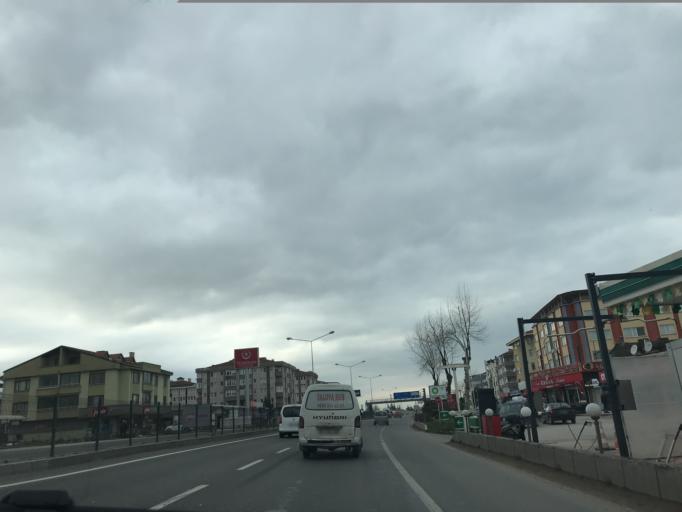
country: TR
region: Yalova
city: Ciftlikkoy
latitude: 40.6623
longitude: 29.3127
